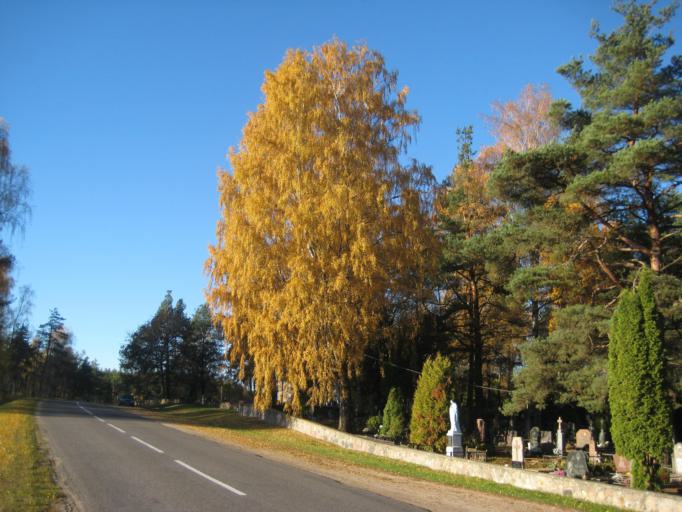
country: LT
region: Utenos apskritis
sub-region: Utena
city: Utena
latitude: 55.5819
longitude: 25.6758
